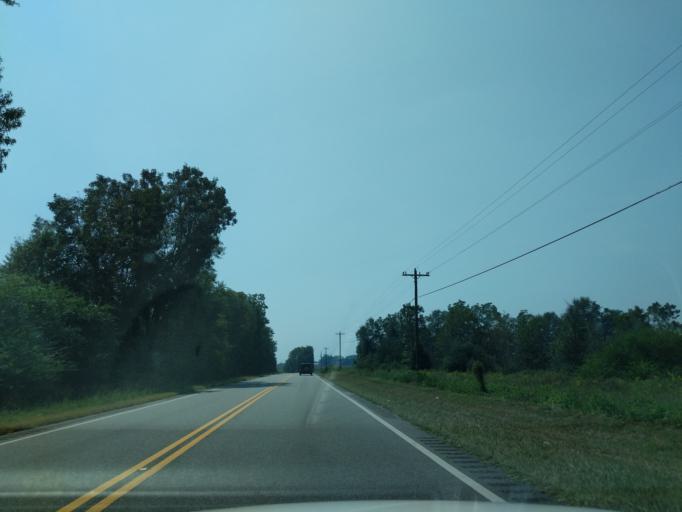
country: US
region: Alabama
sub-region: Covington County
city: Andalusia
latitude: 31.2517
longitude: -86.5216
